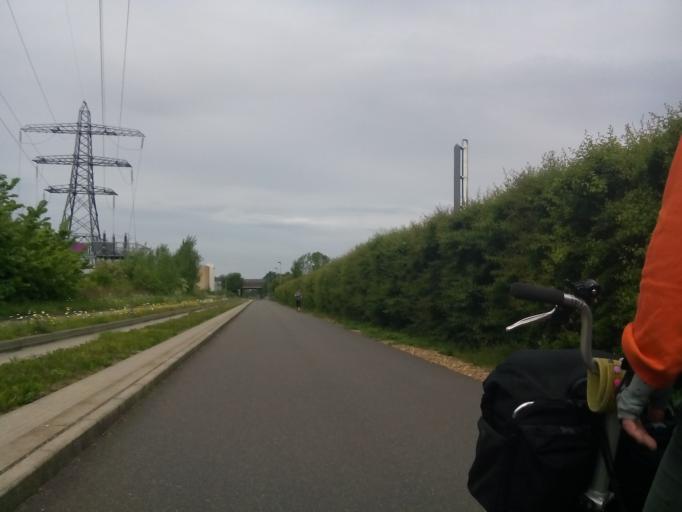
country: GB
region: England
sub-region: Cambridgeshire
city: Histon
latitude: 52.2350
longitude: 0.1322
